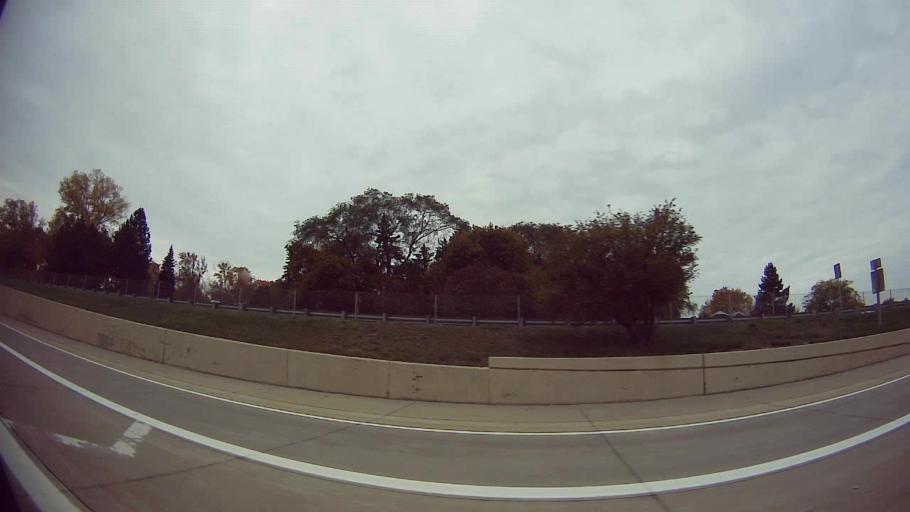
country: US
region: Michigan
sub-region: Oakland County
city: Southfield
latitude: 42.4539
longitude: -83.2145
